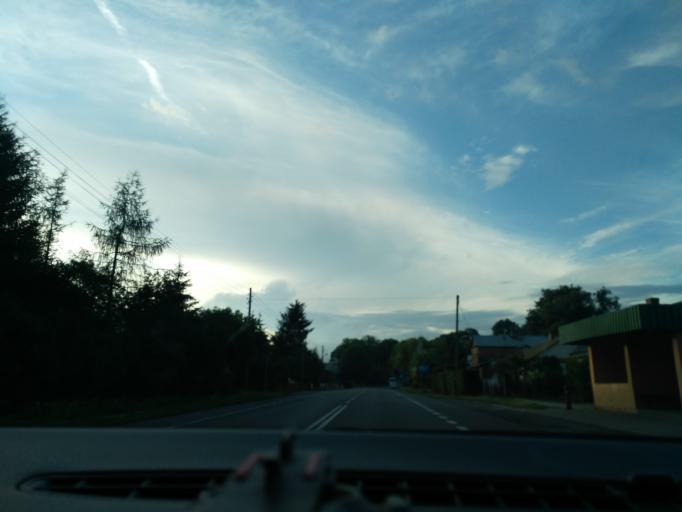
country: PL
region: Lublin Voivodeship
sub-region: Powiat lubelski
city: Niedrzwica Duza
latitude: 51.0892
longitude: 22.3664
